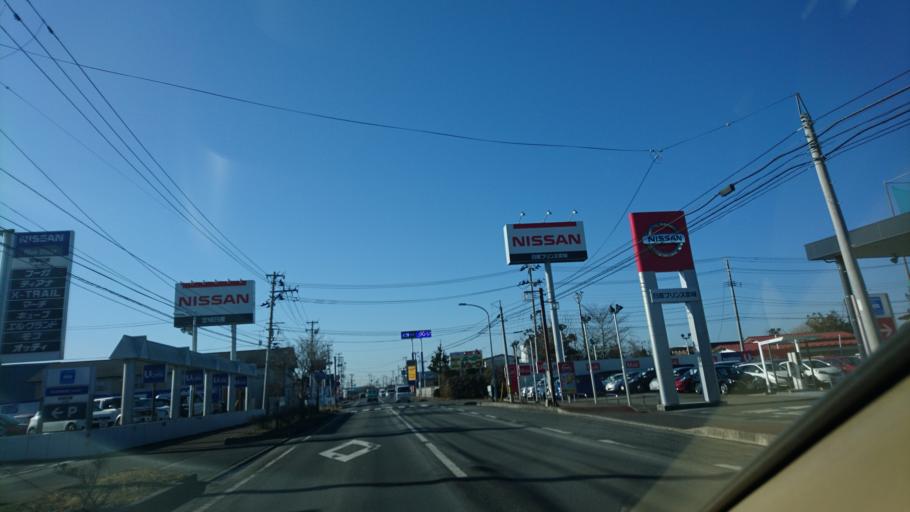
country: JP
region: Miyagi
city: Furukawa
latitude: 38.6003
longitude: 140.9781
